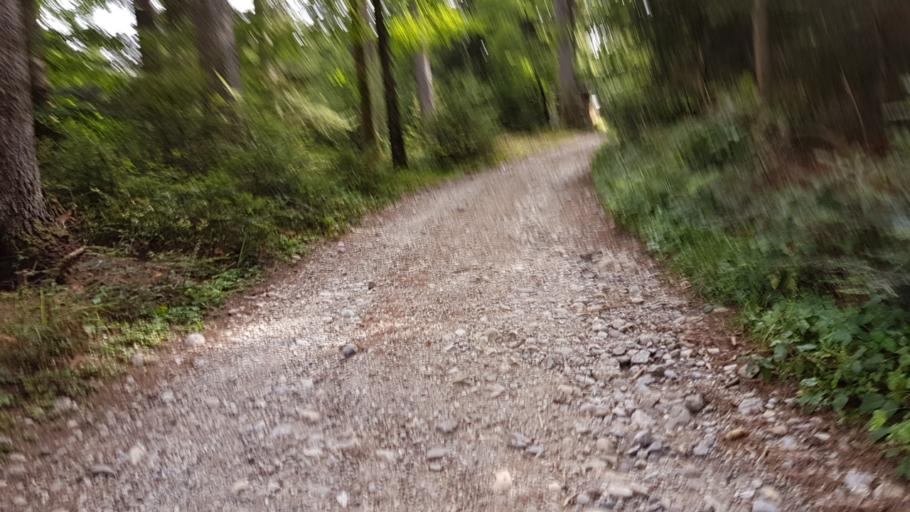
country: CH
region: Lucerne
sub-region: Entlebuch District
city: Oberdiessbach
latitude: 46.8537
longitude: 7.6429
